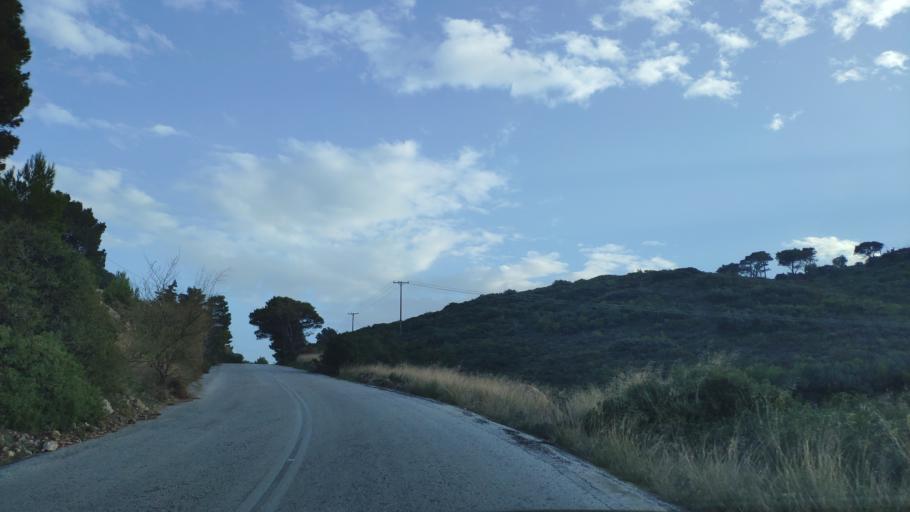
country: GR
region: Attica
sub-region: Nomarchia Anatolikis Attikis
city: Limin Mesoyaias
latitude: 37.9096
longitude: 24.0186
